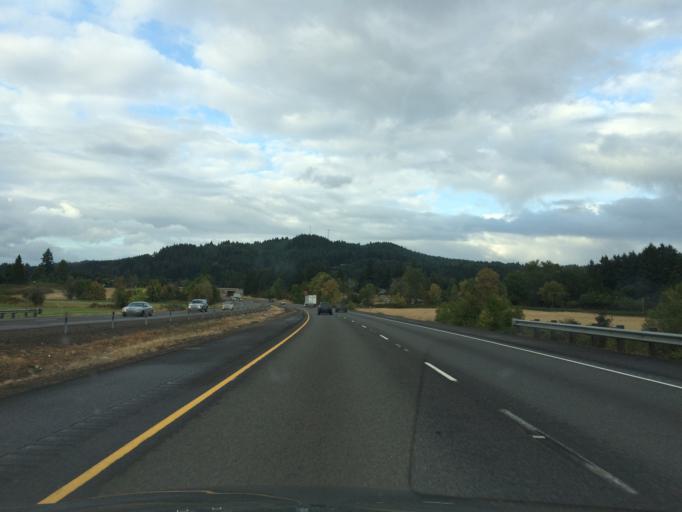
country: US
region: Oregon
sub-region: Lane County
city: Cottage Grove
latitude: 43.7672
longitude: -123.0683
